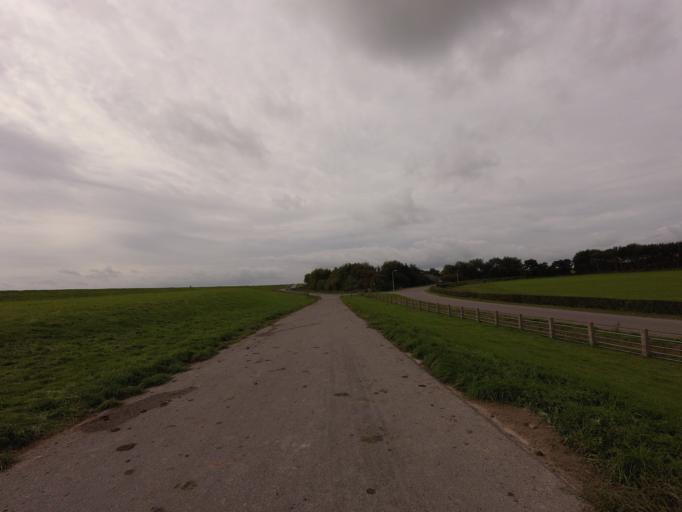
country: NL
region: Friesland
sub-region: Gemeente Ameland
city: Nes
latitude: 53.4402
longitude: 5.7192
